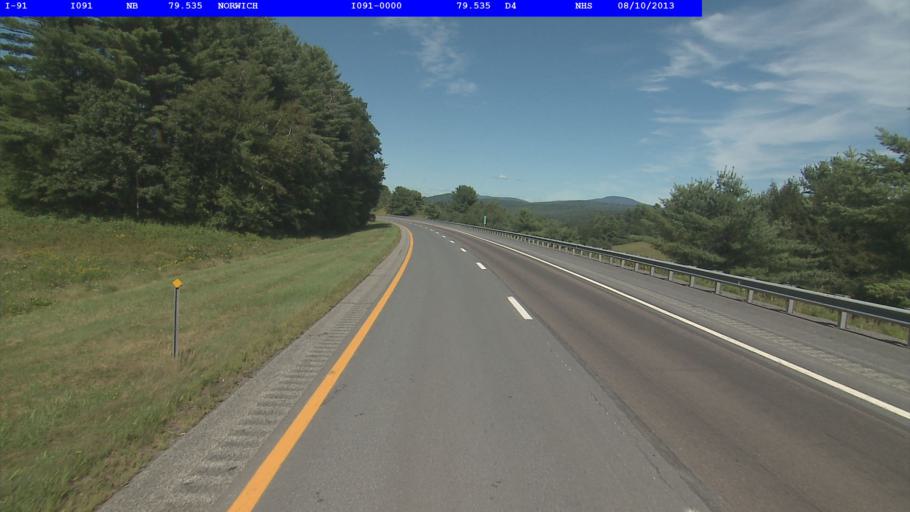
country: US
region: New Hampshire
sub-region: Grafton County
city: Hanover
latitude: 43.7522
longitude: -72.2399
